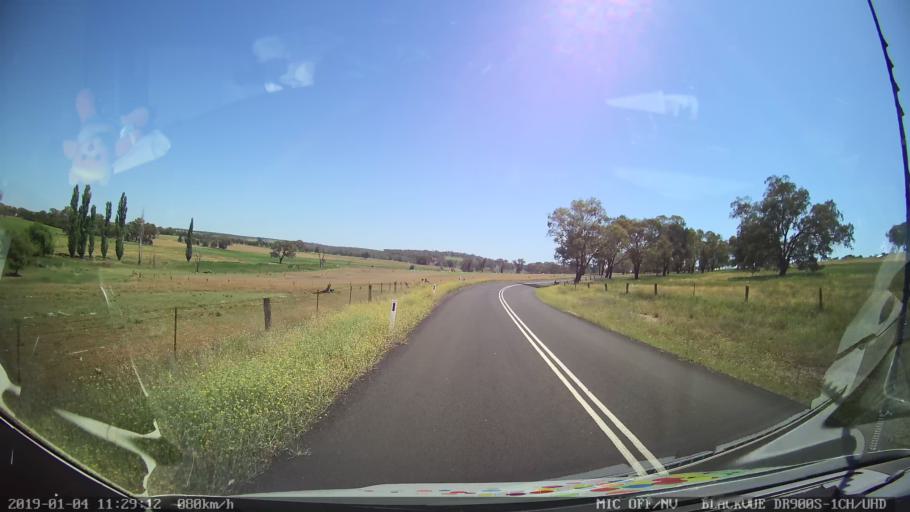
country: AU
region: New South Wales
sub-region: Cabonne
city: Molong
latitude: -33.0905
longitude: 148.7731
